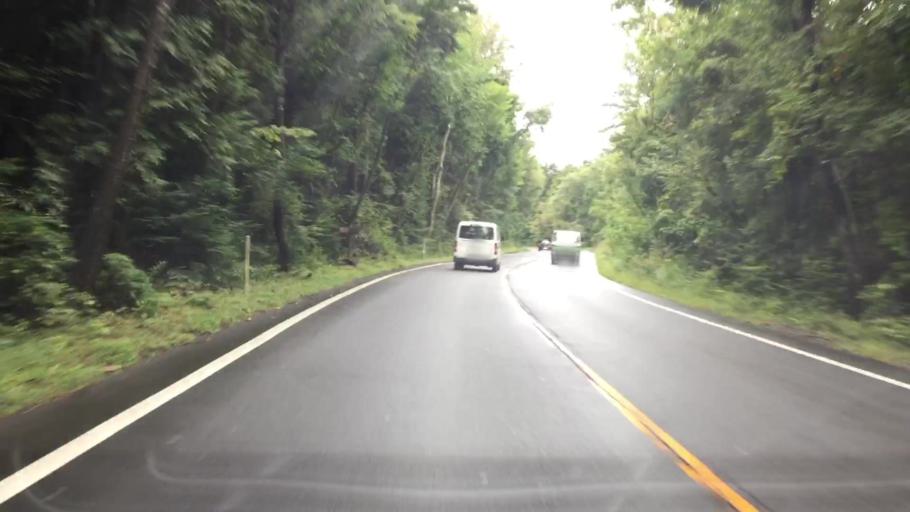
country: JP
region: Yamanashi
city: Fujikawaguchiko
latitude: 35.4697
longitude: 138.6689
